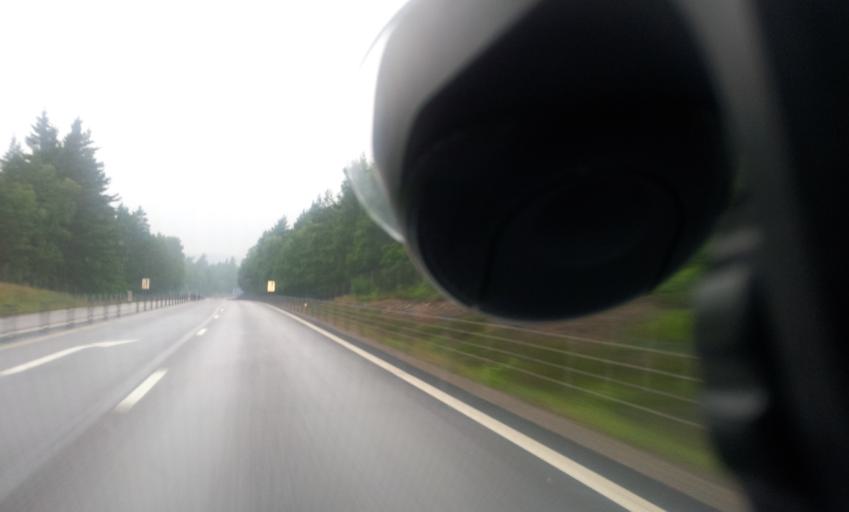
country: SE
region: Kalmar
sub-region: Vasterviks Kommun
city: Gamleby
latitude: 57.8250
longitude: 16.4567
